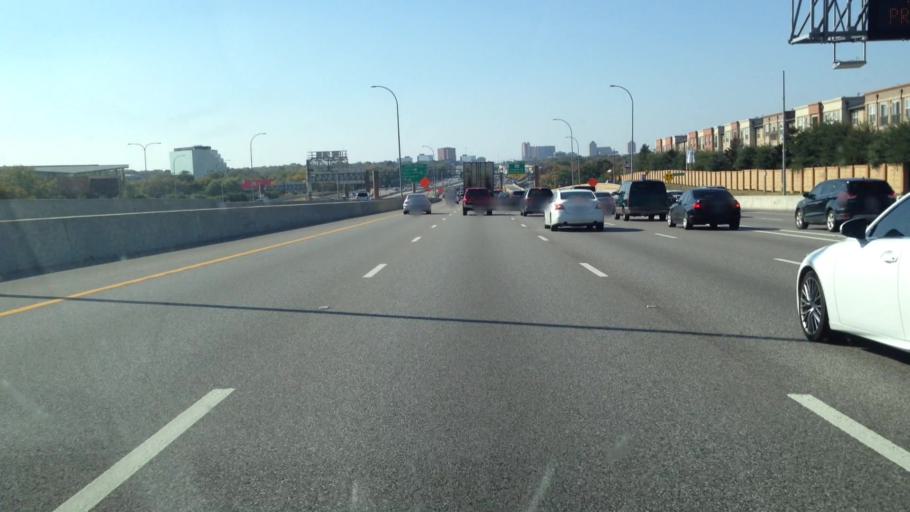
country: US
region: Texas
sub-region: Dallas County
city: Richardson
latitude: 32.9236
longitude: -96.7746
